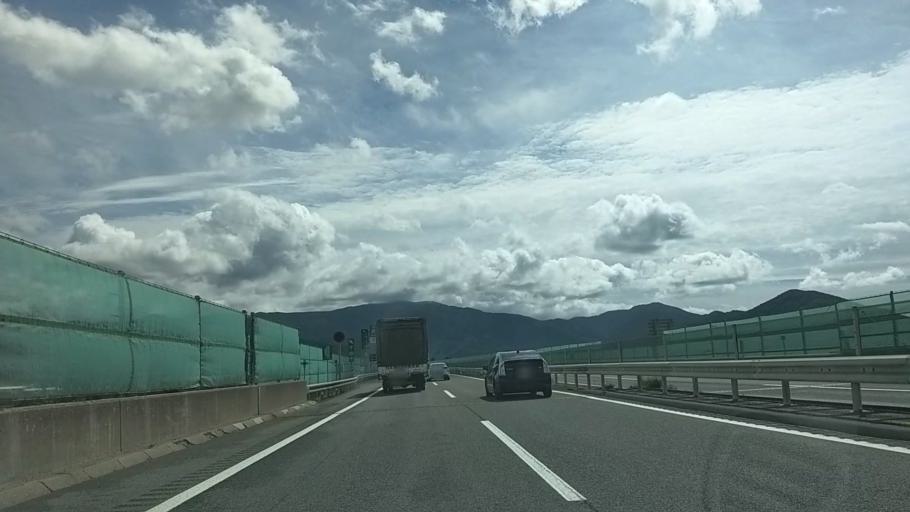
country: JP
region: Nagano
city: Nagano-shi
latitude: 36.5559
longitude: 138.1230
